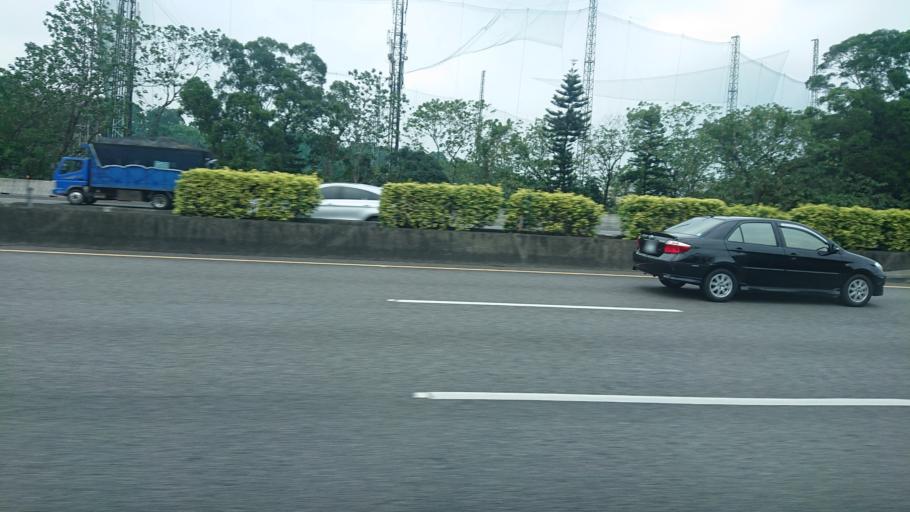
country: TW
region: Taipei
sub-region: Taipei
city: Banqiao
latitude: 24.9750
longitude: 121.4514
